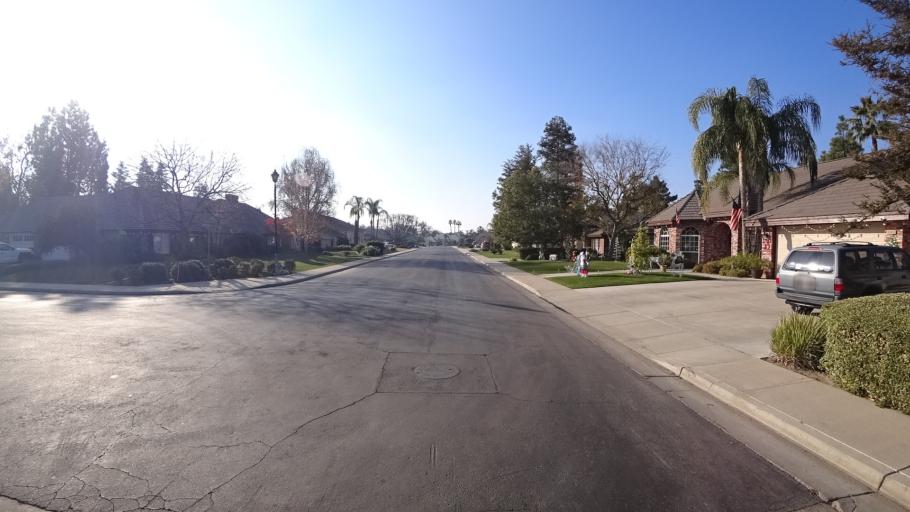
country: US
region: California
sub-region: Kern County
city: Greenacres
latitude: 35.3391
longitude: -119.1030
